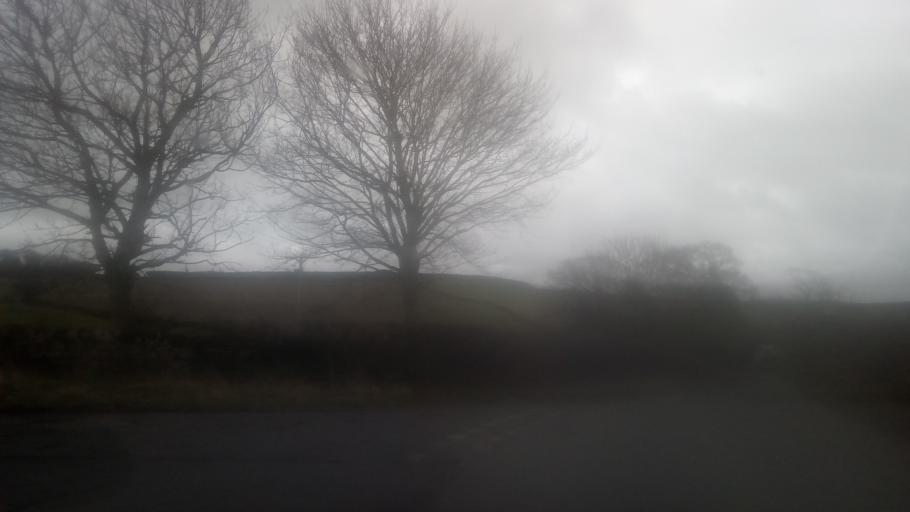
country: GB
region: Scotland
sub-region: The Scottish Borders
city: Jedburgh
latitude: 55.4686
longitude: -2.4856
